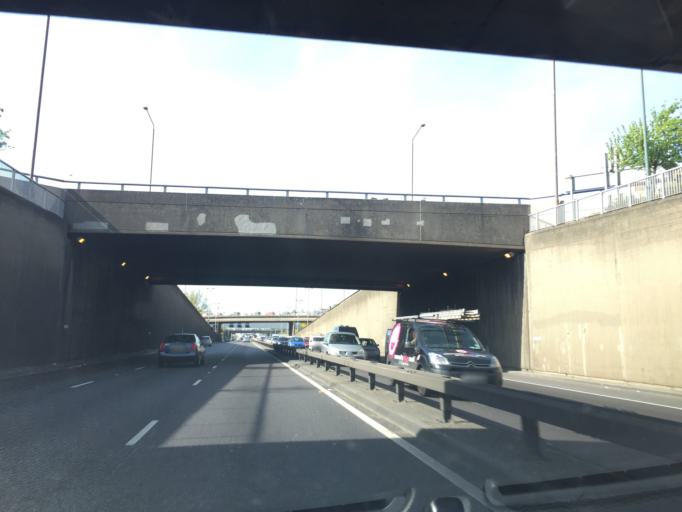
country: GB
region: England
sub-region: Greater London
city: Blackheath
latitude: 51.4746
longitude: 0.0246
